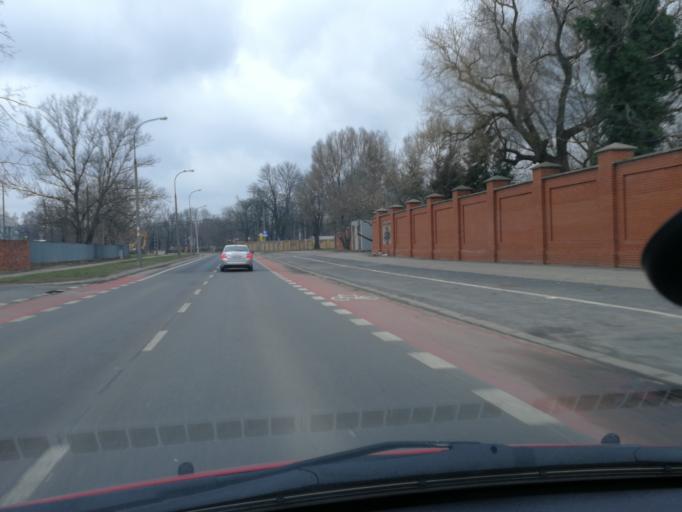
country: PL
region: Masovian Voivodeship
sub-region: Warszawa
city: Wola
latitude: 52.2512
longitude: 20.9648
